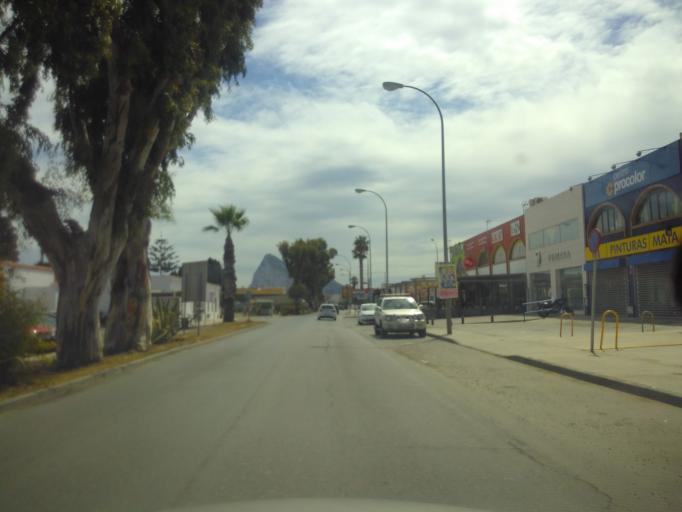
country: ES
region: Andalusia
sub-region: Provincia de Cadiz
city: La Linea de la Concepcion
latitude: 36.1835
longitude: -5.3496
